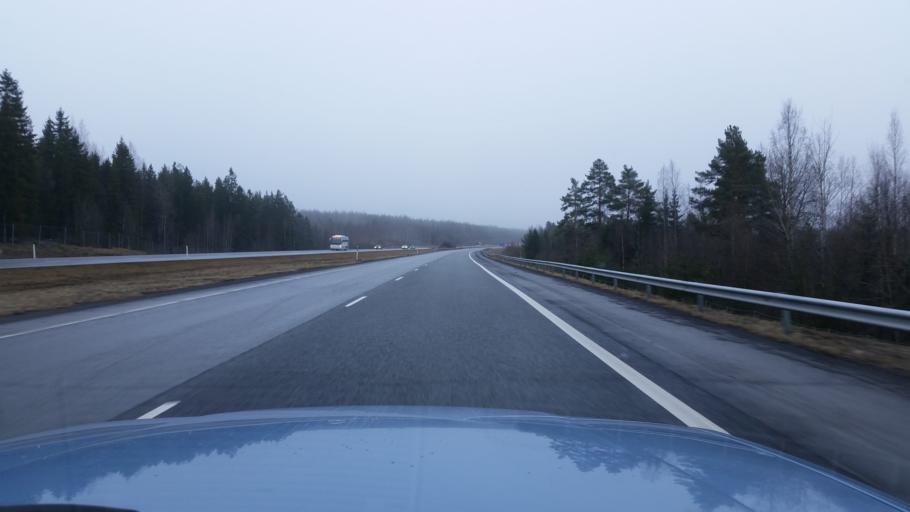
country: FI
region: Pirkanmaa
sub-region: Etelae-Pirkanmaa
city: Viiala
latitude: 61.2708
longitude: 23.8183
